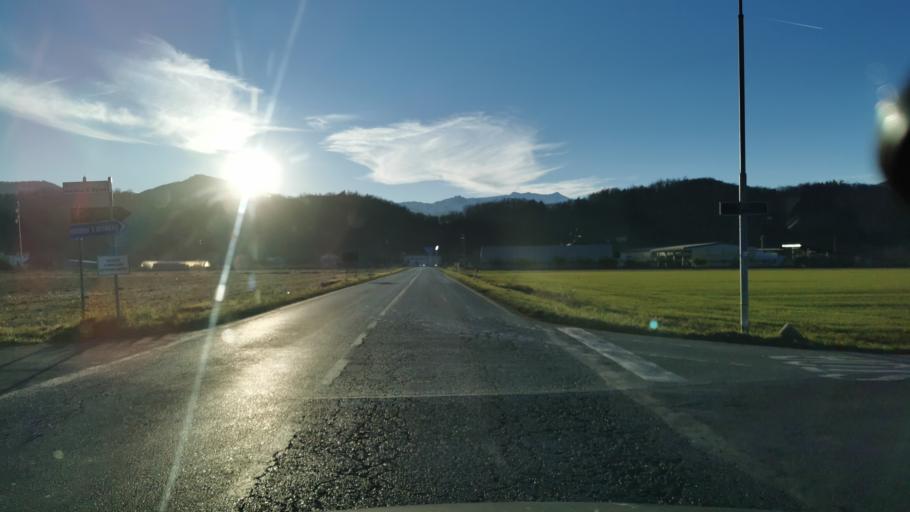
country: IT
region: Piedmont
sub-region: Provincia di Cuneo
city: Caraglio
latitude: 44.4282
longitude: 7.4351
